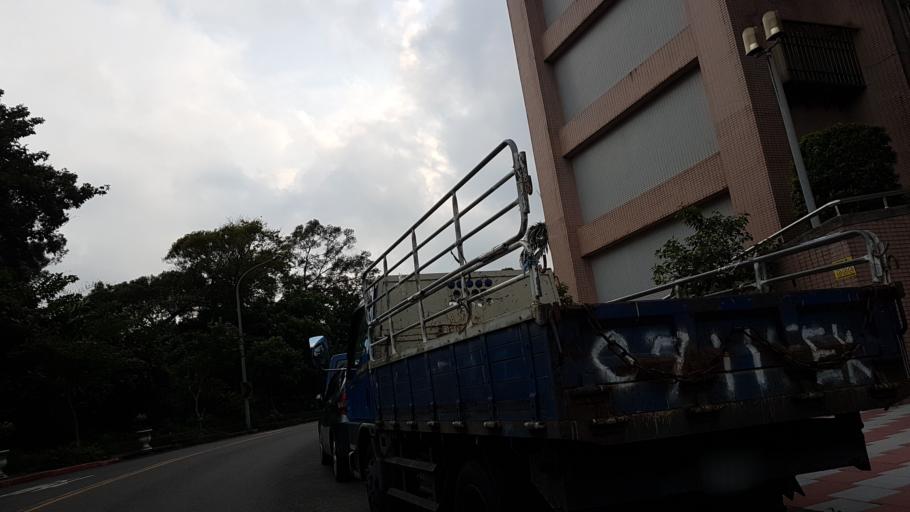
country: TW
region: Taipei
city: Taipei
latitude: 25.0036
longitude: 121.5712
